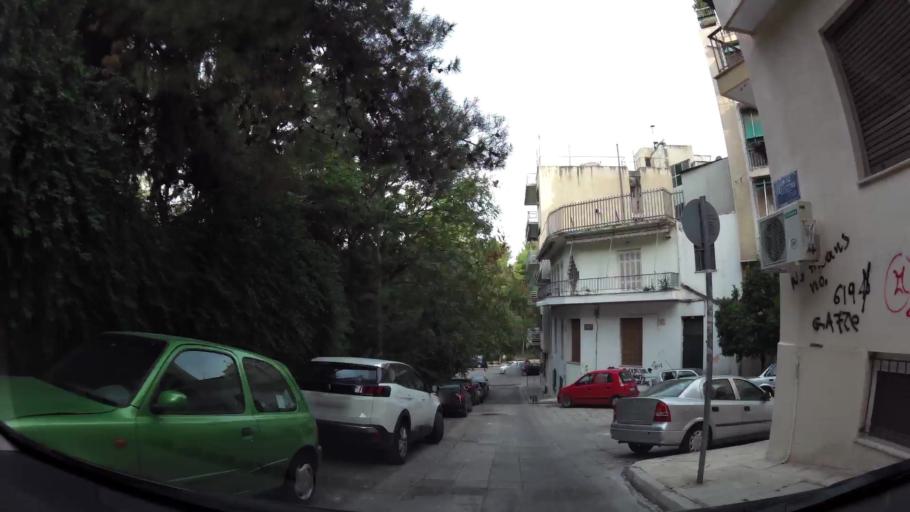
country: GR
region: Attica
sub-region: Nomarchia Athinas
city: Kipseli
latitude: 37.9927
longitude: 23.7425
